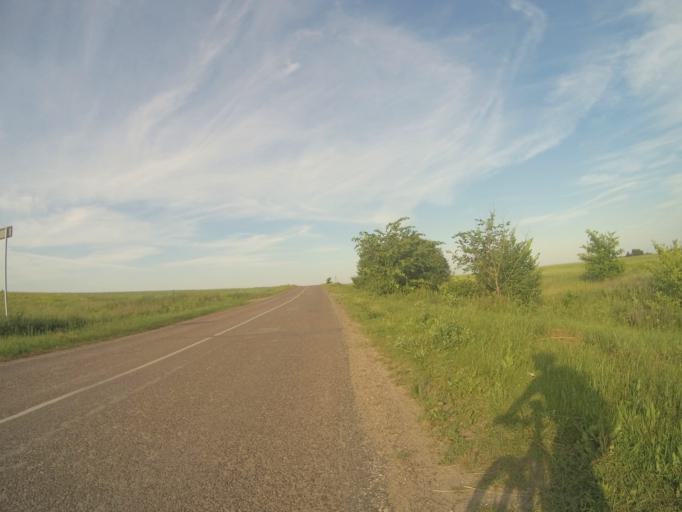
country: RU
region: Vladimir
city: Suzdal'
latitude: 56.3709
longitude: 40.4391
